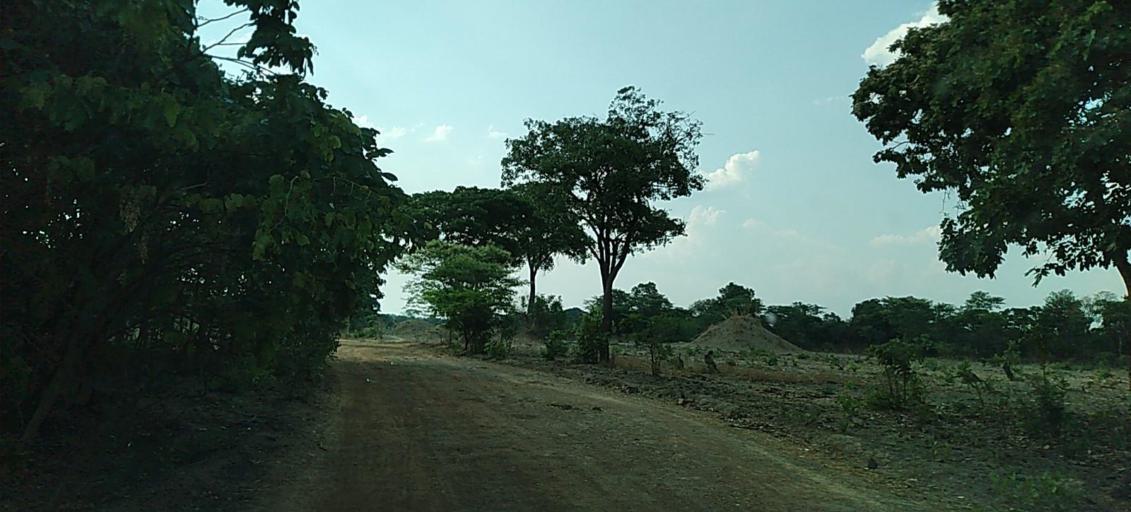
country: ZM
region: Copperbelt
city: Mpongwe
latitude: -13.4771
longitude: 28.0824
